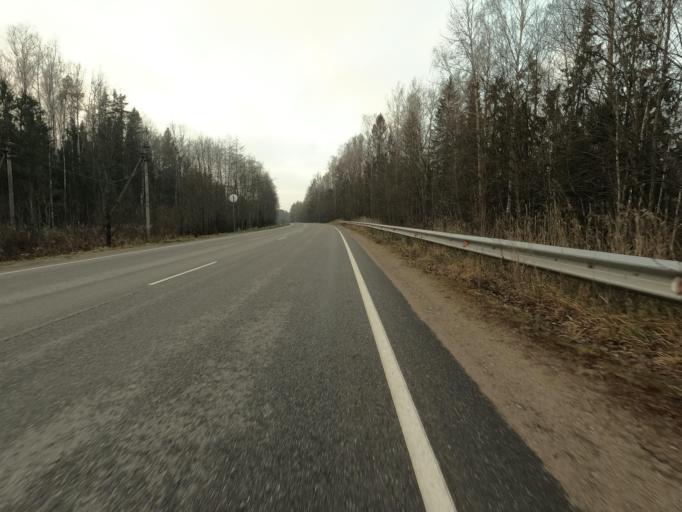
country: RU
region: Leningrad
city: Kirovsk
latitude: 59.8191
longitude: 30.9762
